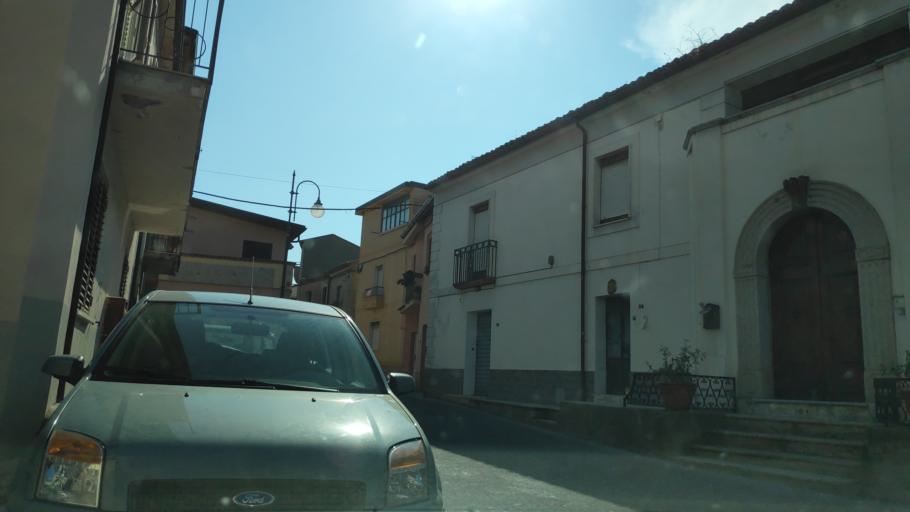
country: IT
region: Calabria
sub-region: Provincia di Catanzaro
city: Soverato Superiore
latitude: 38.6883
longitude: 16.5307
